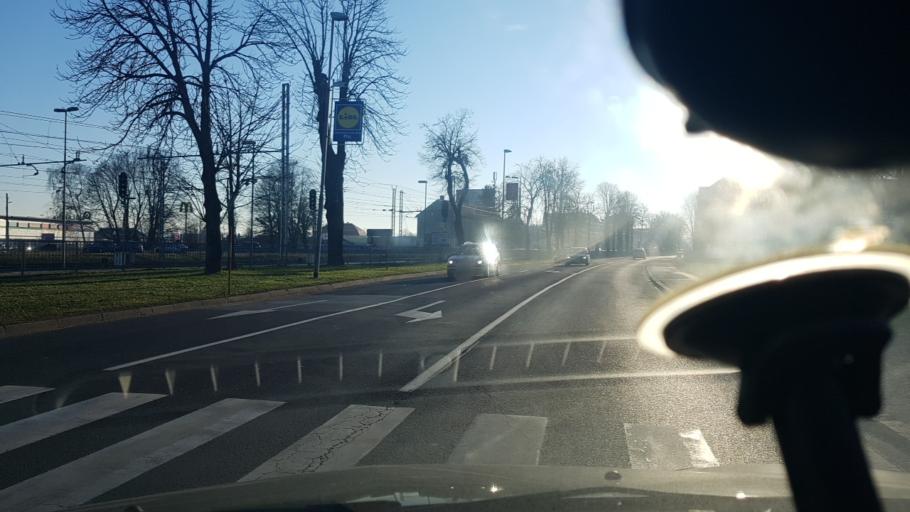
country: SI
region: Ptuj
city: Ptuj
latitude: 46.4215
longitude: 15.8774
